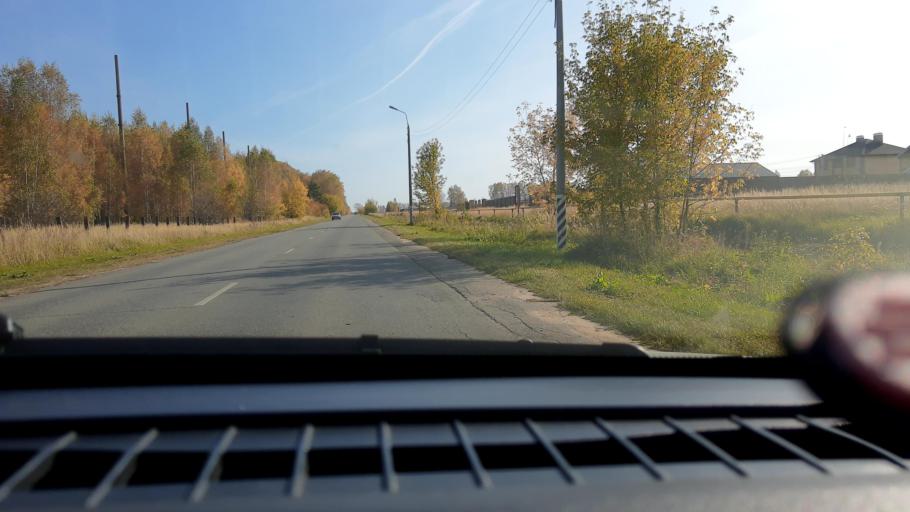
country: RU
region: Nizjnij Novgorod
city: Kstovo
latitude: 56.1549
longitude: 44.2751
